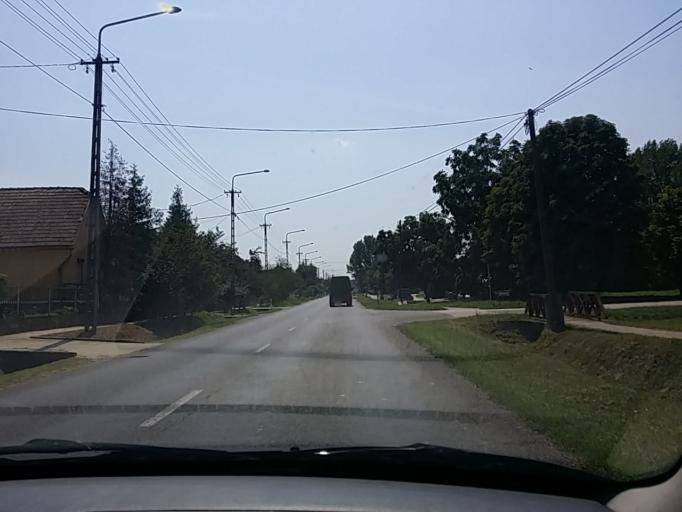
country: HU
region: Tolna
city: Iregszemcse
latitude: 46.7070
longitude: 18.1771
